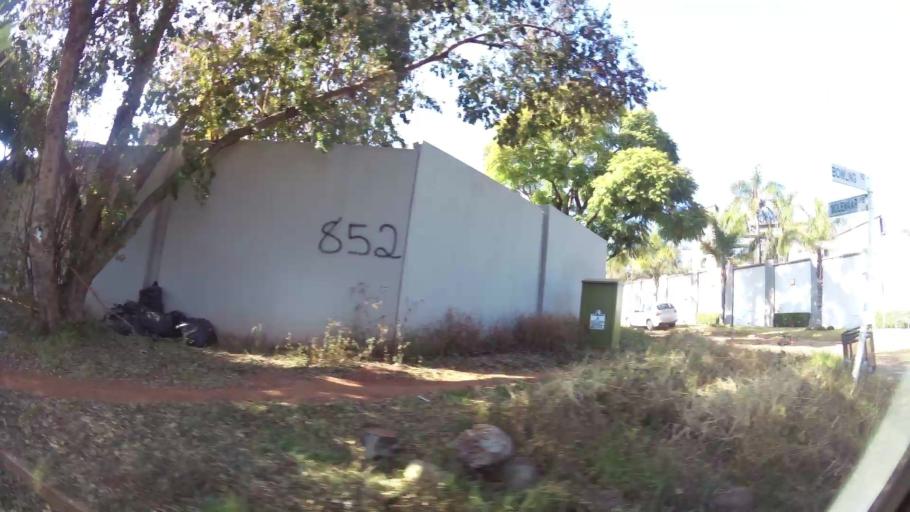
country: ZA
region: Gauteng
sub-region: Ekurhuleni Metropolitan Municipality
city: Germiston
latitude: -26.1747
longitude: 28.1511
